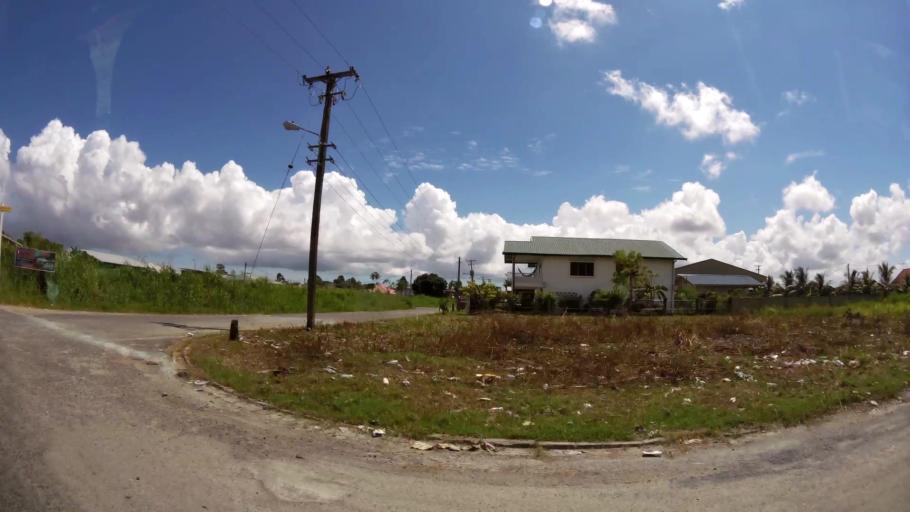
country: SR
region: Paramaribo
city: Paramaribo
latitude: 5.8596
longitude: -55.1293
